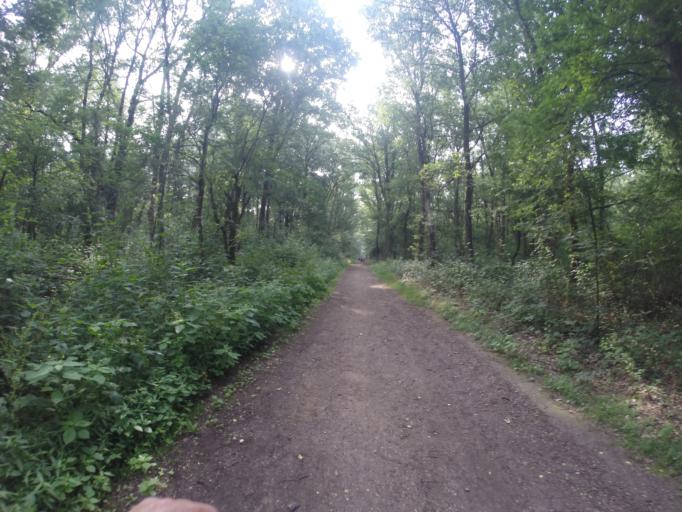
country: DE
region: North Rhine-Westphalia
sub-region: Regierungsbezirk Dusseldorf
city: Emmerich
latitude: 51.8712
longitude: 6.1861
